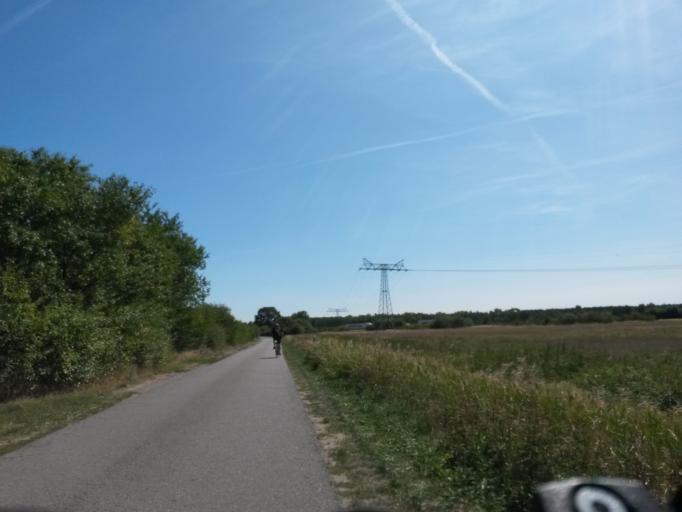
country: DE
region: Saxony-Anhalt
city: Tangermunde
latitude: 52.5735
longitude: 11.9627
